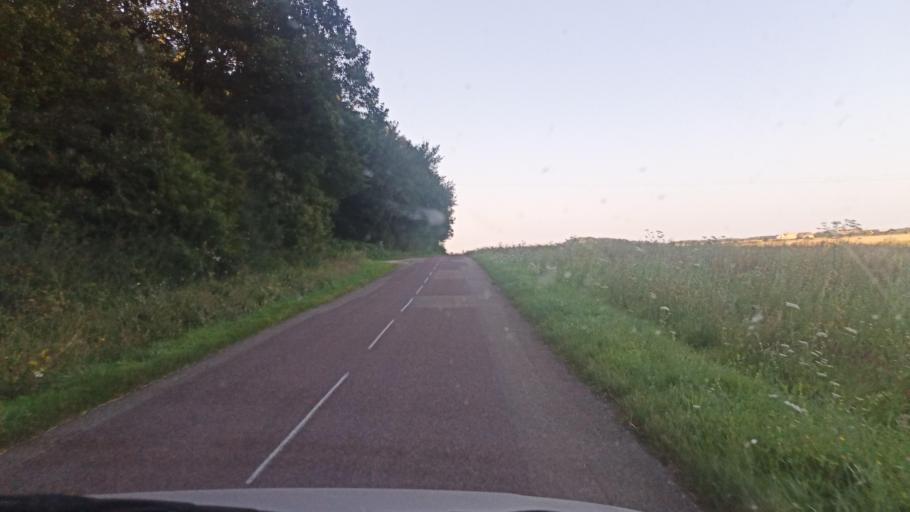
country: FR
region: Bourgogne
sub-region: Departement de l'Yonne
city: Saint-Valerien
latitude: 48.2169
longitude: 3.1229
